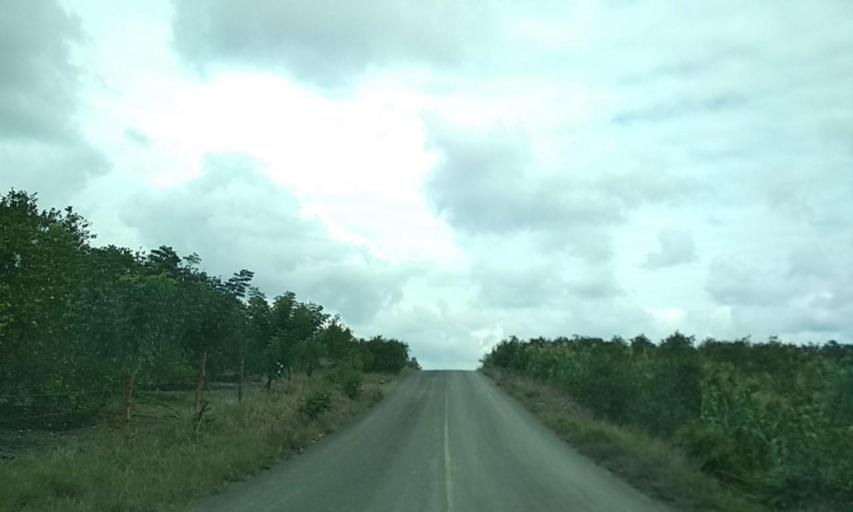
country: MX
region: Veracruz
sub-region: Papantla
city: El Chote
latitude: 20.3442
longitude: -97.3898
